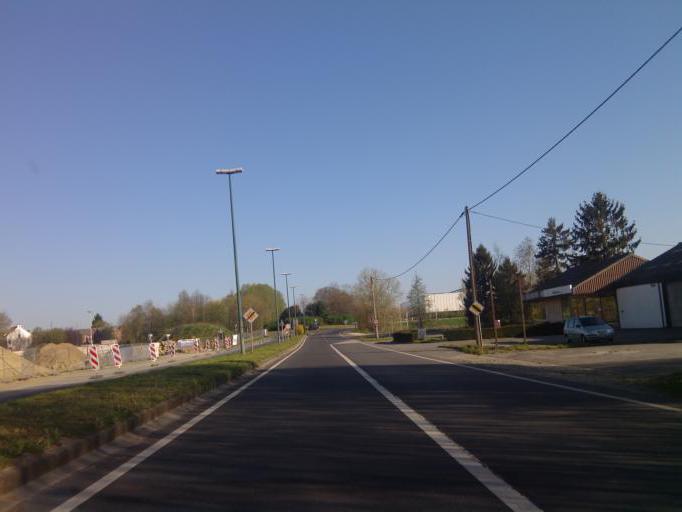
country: BE
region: Wallonia
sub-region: Province du Brabant Wallon
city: Louvain-la-Neuve
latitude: 50.6735
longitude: 4.6244
